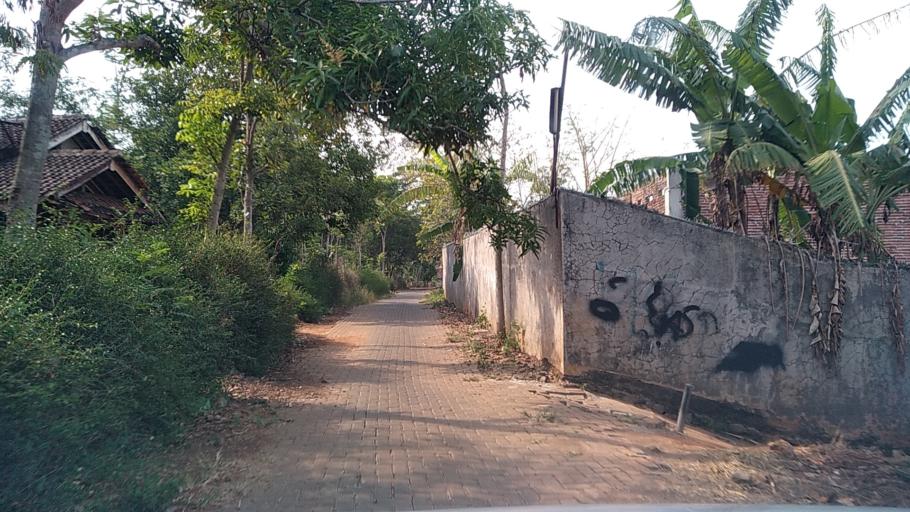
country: ID
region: Central Java
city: Semarang
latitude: -7.0510
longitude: 110.3111
